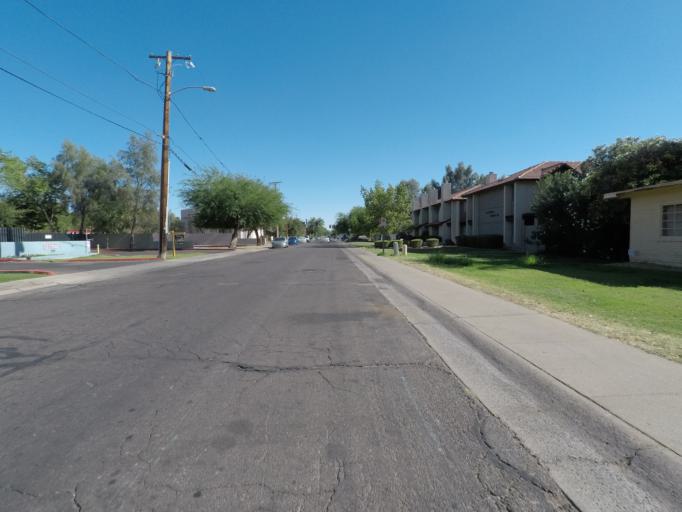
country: US
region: Arizona
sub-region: Maricopa County
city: Tempe Junction
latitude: 33.4231
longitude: -111.9473
